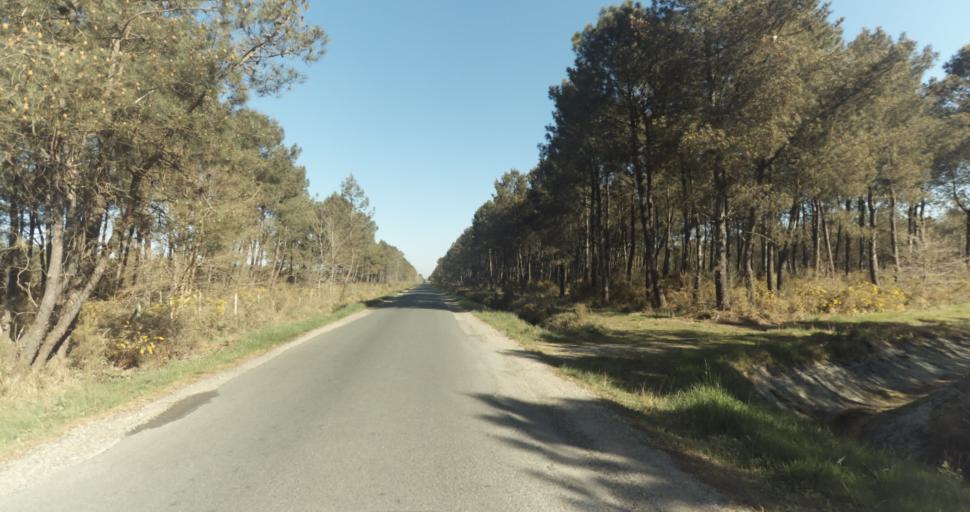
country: FR
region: Aquitaine
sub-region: Departement de la Gironde
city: Marcheprime
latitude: 44.7564
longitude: -0.8507
